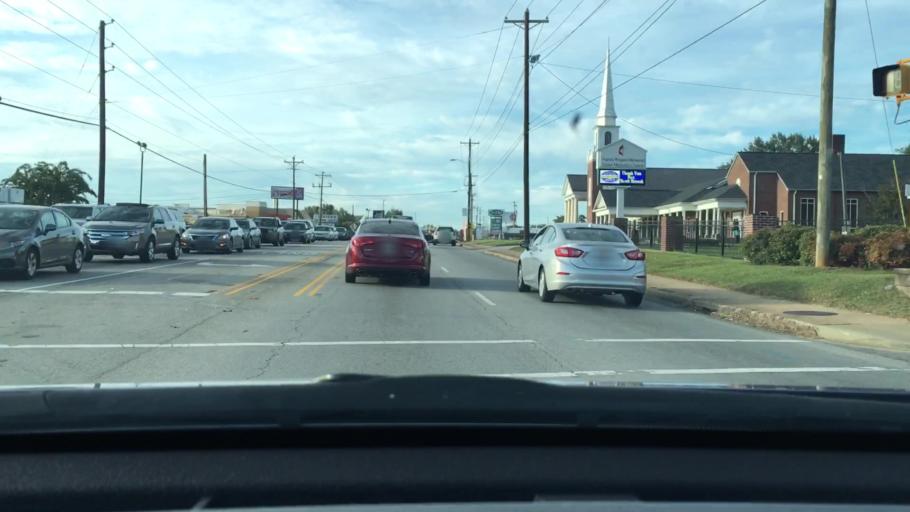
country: US
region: South Carolina
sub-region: Lexington County
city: West Columbia
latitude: 34.0309
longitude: -81.0867
